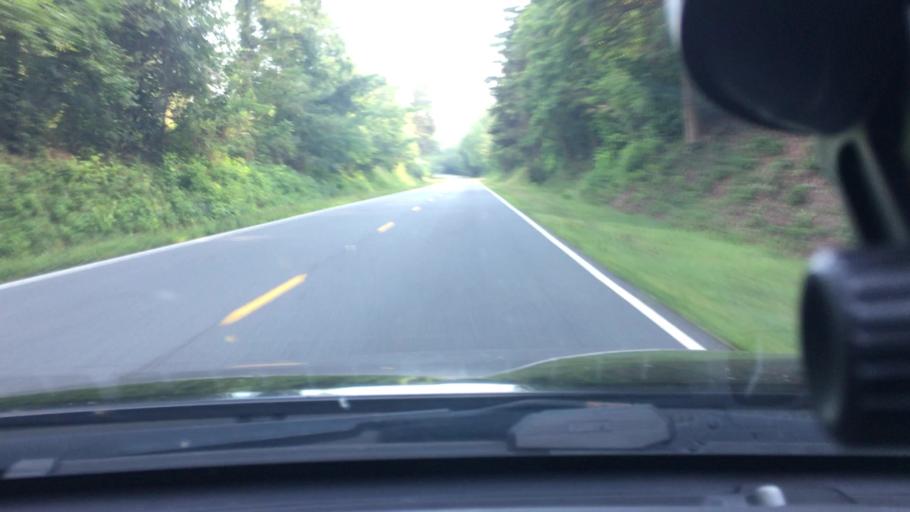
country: US
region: North Carolina
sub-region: Rutherford County
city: Rutherfordton
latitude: 35.5031
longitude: -81.9765
